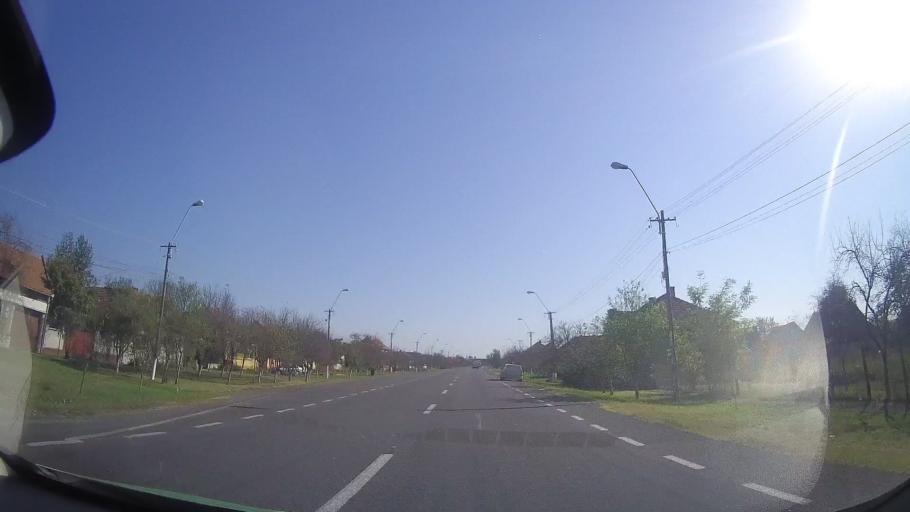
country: RO
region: Timis
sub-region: Comuna Belint
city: Belint
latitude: 45.7540
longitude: 21.7523
